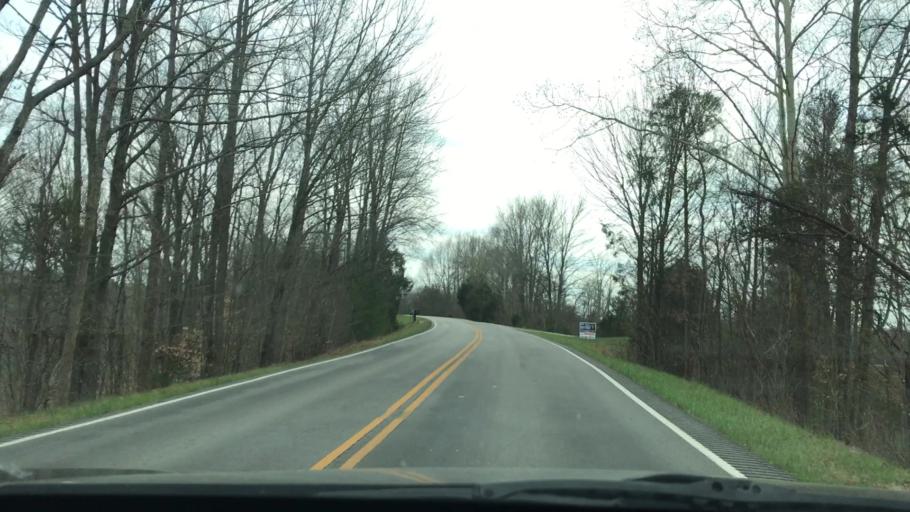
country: US
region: Kentucky
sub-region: Hart County
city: Munfordville
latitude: 37.3051
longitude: -85.7642
